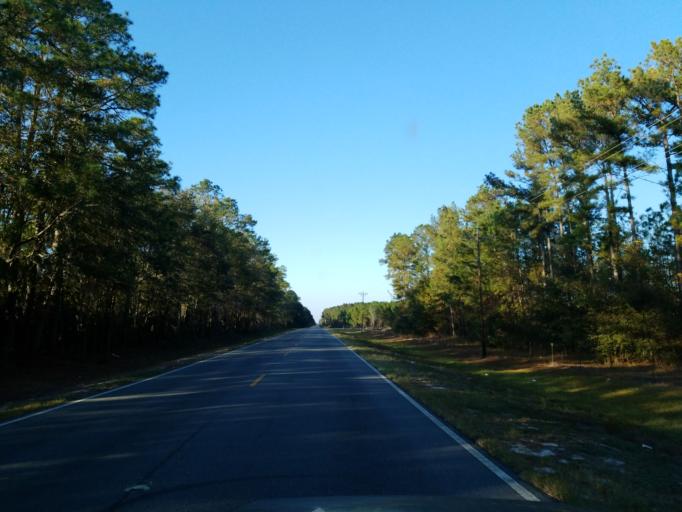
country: US
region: Georgia
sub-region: Lanier County
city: Lakeland
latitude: 31.0660
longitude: -83.0722
